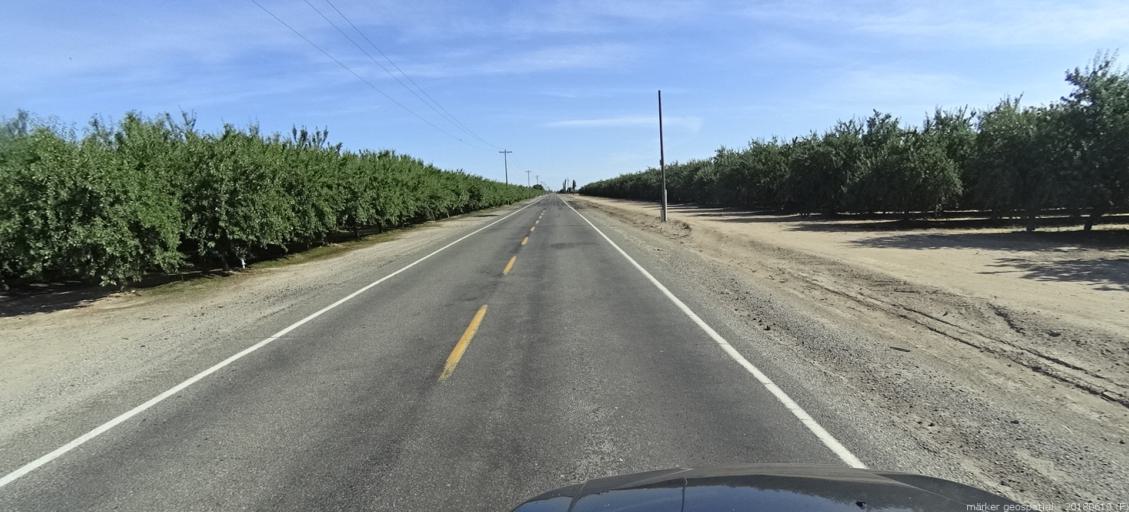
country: US
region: California
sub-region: Madera County
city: Fairmead
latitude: 37.0446
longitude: -120.2568
